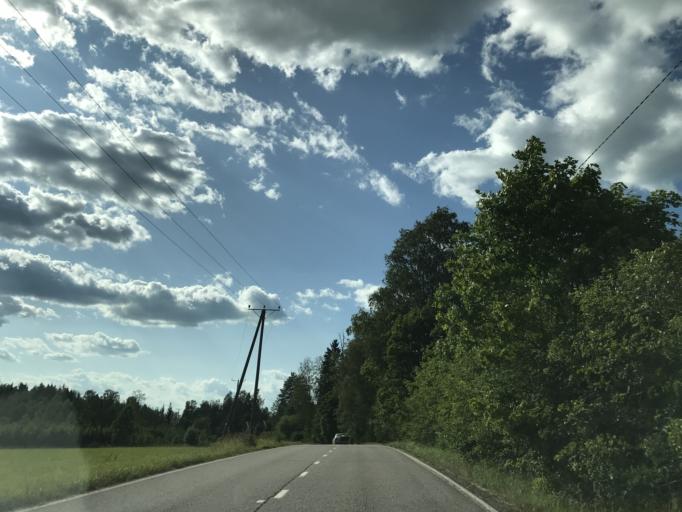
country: FI
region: Uusimaa
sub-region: Helsinki
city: Nurmijaervi
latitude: 60.4497
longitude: 24.6814
